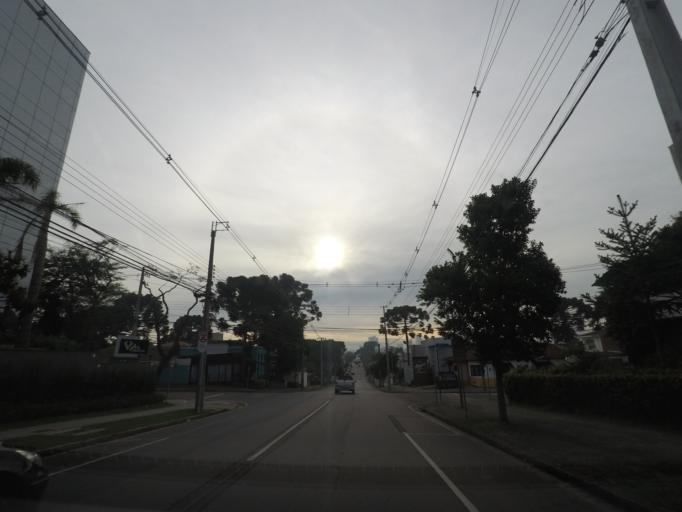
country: BR
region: Parana
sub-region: Curitiba
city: Curitiba
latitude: -25.4410
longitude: -49.2966
